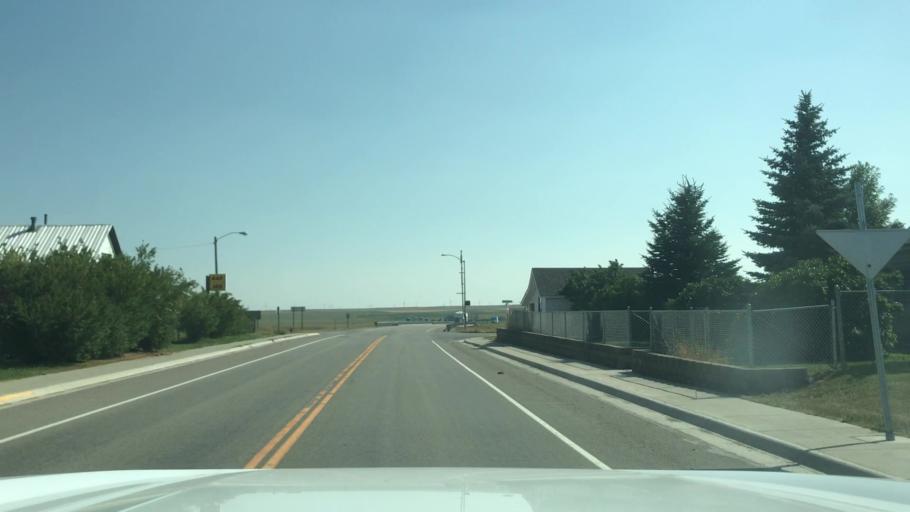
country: US
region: Montana
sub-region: Wheatland County
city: Harlowton
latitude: 46.6758
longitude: -109.7524
